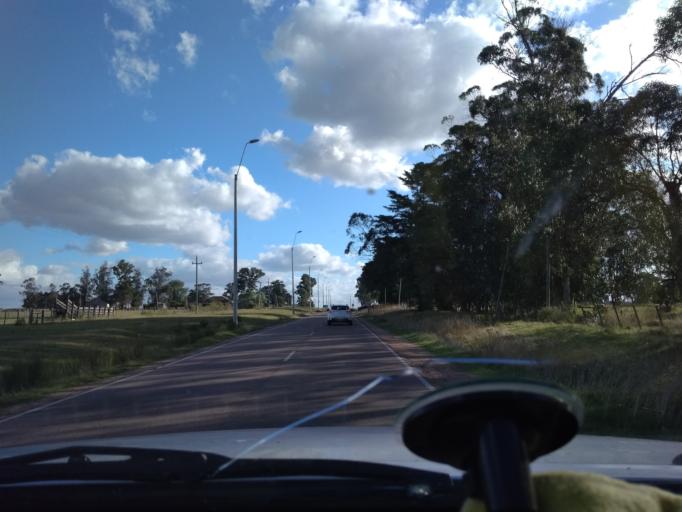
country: UY
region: Canelones
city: Tala
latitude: -34.3574
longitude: -55.7728
